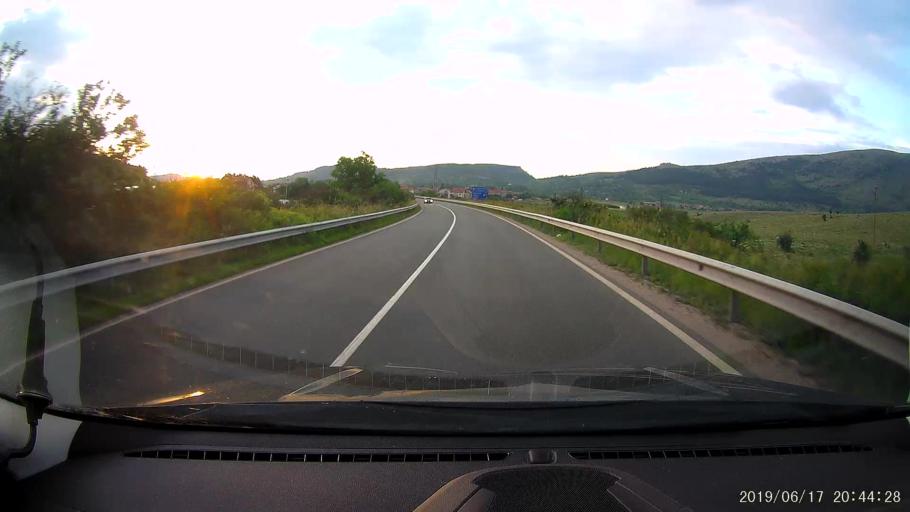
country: BG
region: Sofiya
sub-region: Obshtina Dragoman
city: Dragoman
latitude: 42.9273
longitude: 22.9353
